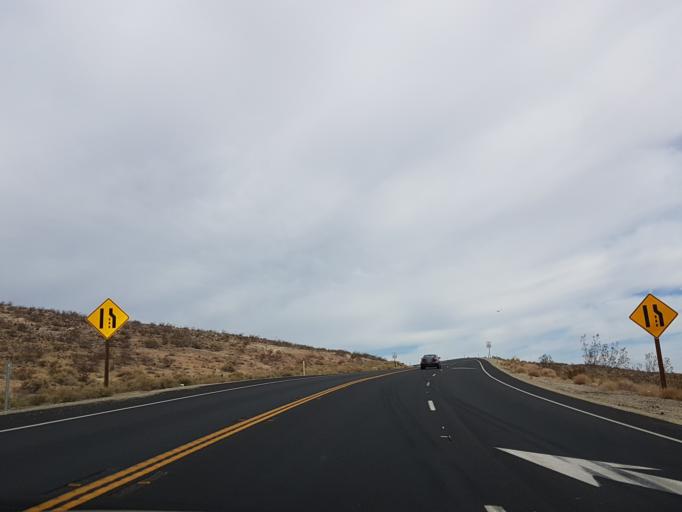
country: US
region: California
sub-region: Kern County
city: Ridgecrest
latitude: 35.4503
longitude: -117.6571
